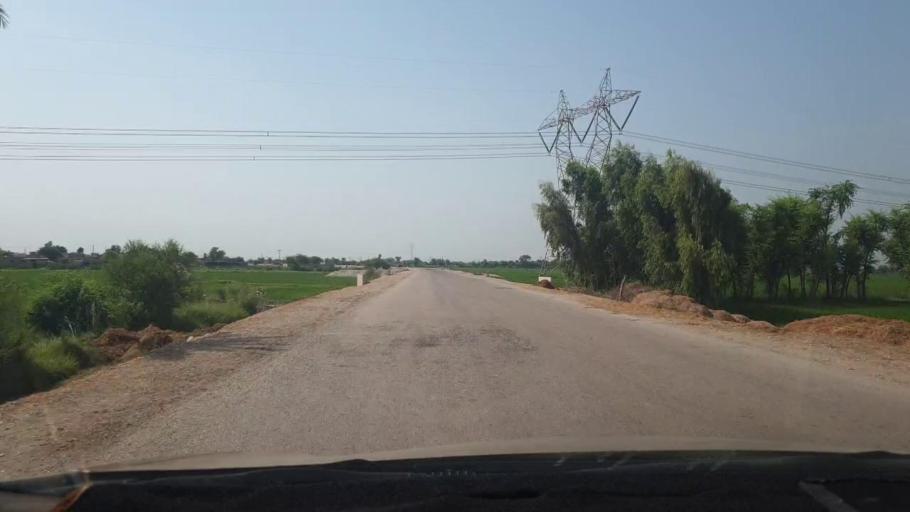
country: PK
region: Sindh
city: Larkana
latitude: 27.6075
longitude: 68.2397
